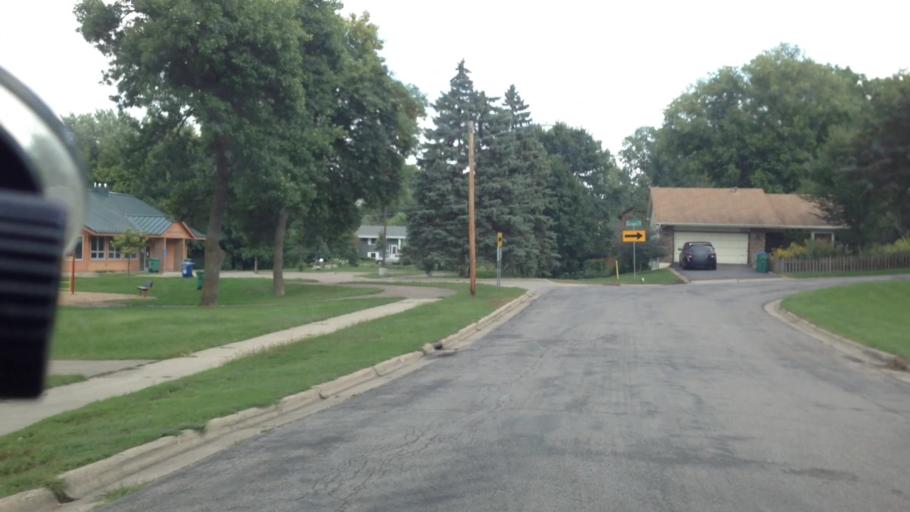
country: US
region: Minnesota
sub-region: Hennepin County
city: Saint Louis Park
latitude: 44.9533
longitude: -93.3551
